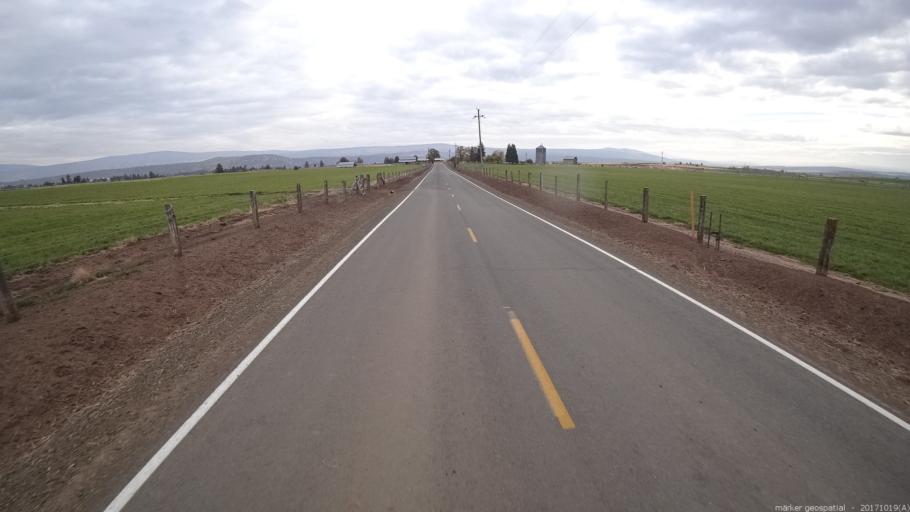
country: US
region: California
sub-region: Shasta County
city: Burney
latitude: 41.0299
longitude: -121.3421
